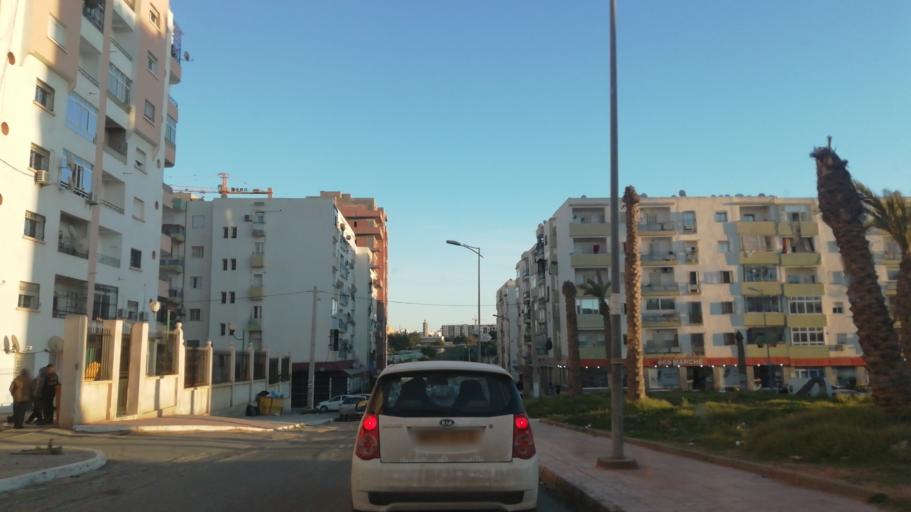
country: DZ
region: Oran
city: Bir el Djir
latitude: 35.7173
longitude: -0.5754
